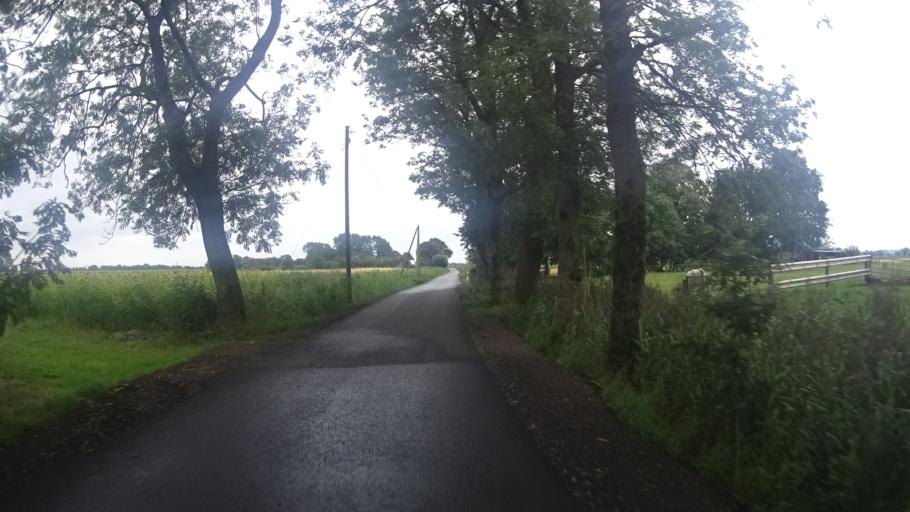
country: DE
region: Schleswig-Holstein
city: Altenmoor
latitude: 53.7807
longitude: 9.5501
